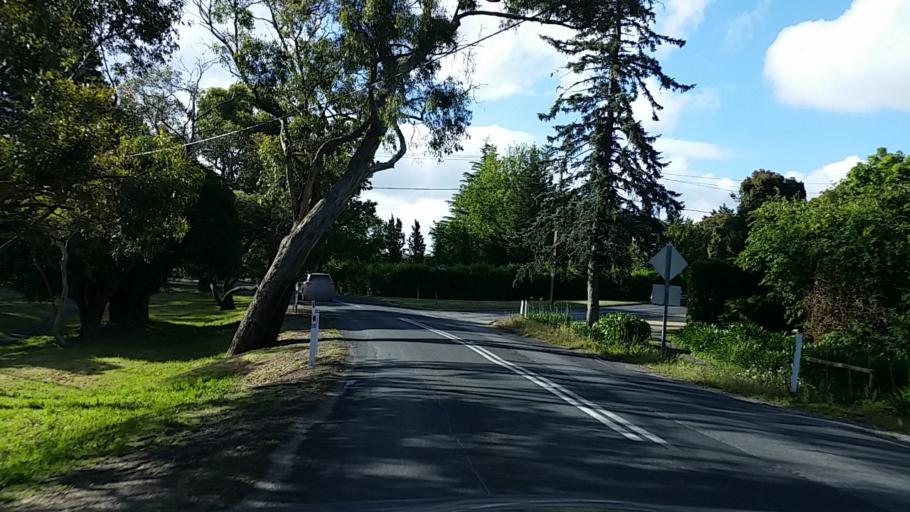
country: AU
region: South Australia
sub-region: Adelaide Hills
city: Stirling
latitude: -35.0179
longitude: 138.7501
